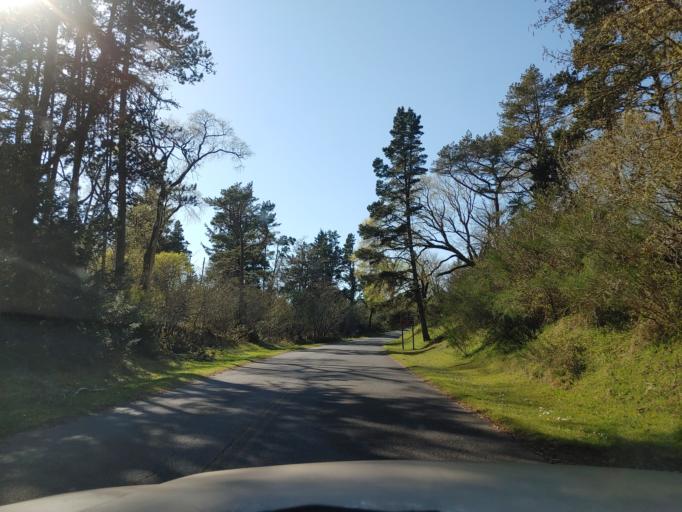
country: US
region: Oregon
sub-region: Clatsop County
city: Warrenton
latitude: 46.1793
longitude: -123.9679
